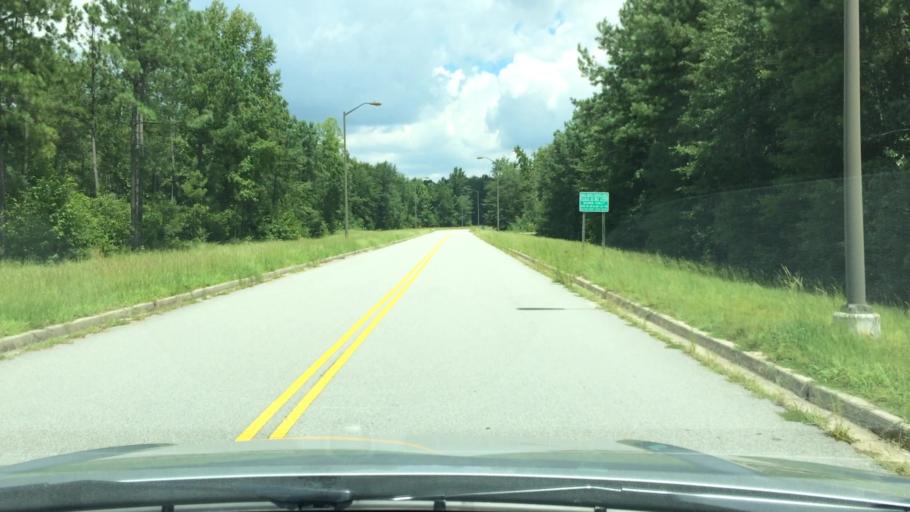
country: US
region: South Carolina
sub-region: Calhoun County
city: Oak Grove
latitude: 33.7992
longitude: -81.0043
